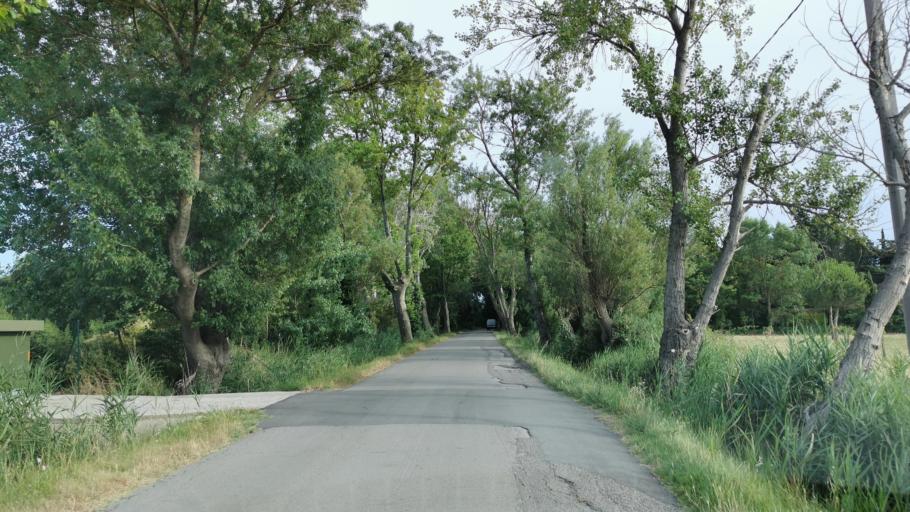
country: FR
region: Languedoc-Roussillon
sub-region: Departement de l'Aude
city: Narbonne
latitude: 43.2037
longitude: 2.9988
